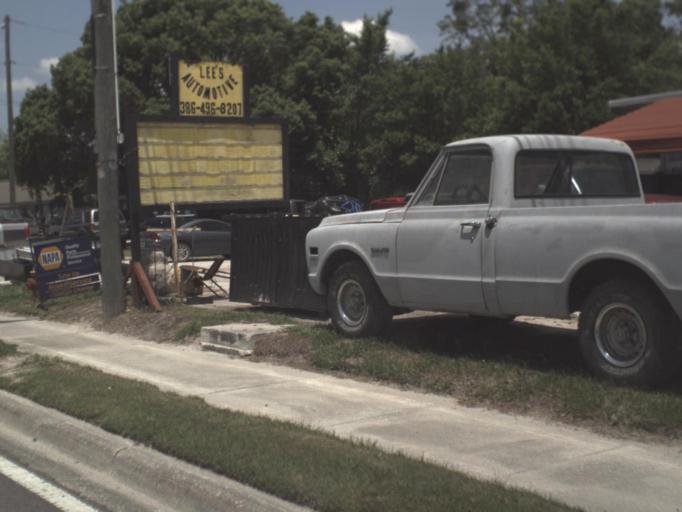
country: US
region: Florida
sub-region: Union County
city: Lake Butler
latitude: 30.0236
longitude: -82.3291
